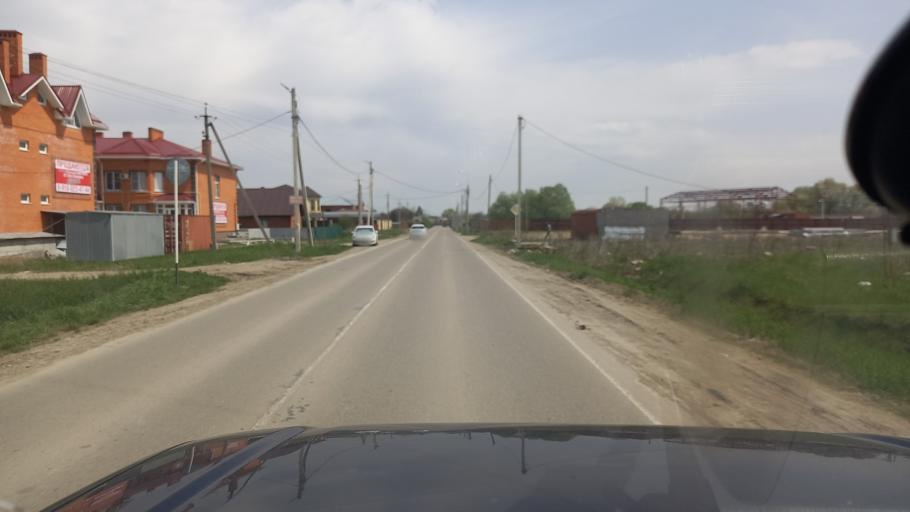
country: RU
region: Adygeya
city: Yablonovskiy
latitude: 44.9877
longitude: 38.9921
